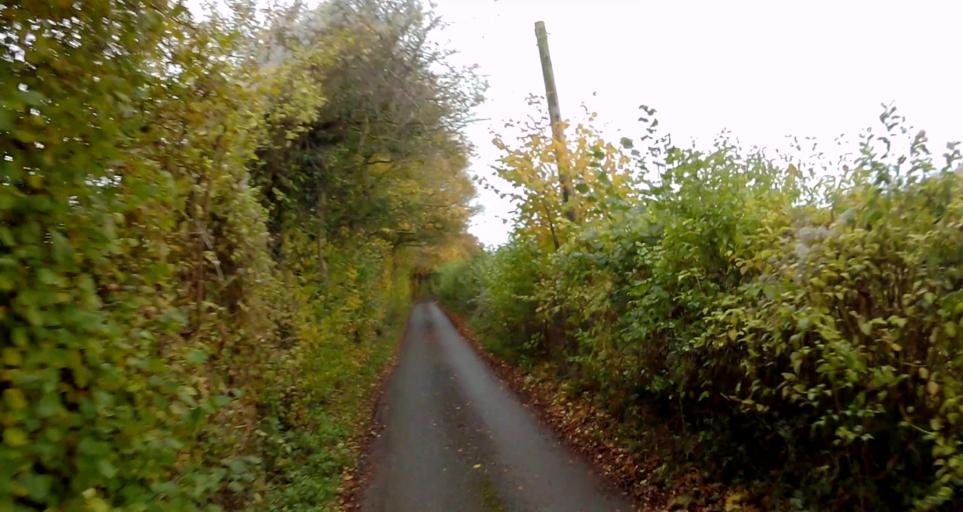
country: GB
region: England
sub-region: Hampshire
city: Long Sutton
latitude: 51.2362
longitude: -0.8930
